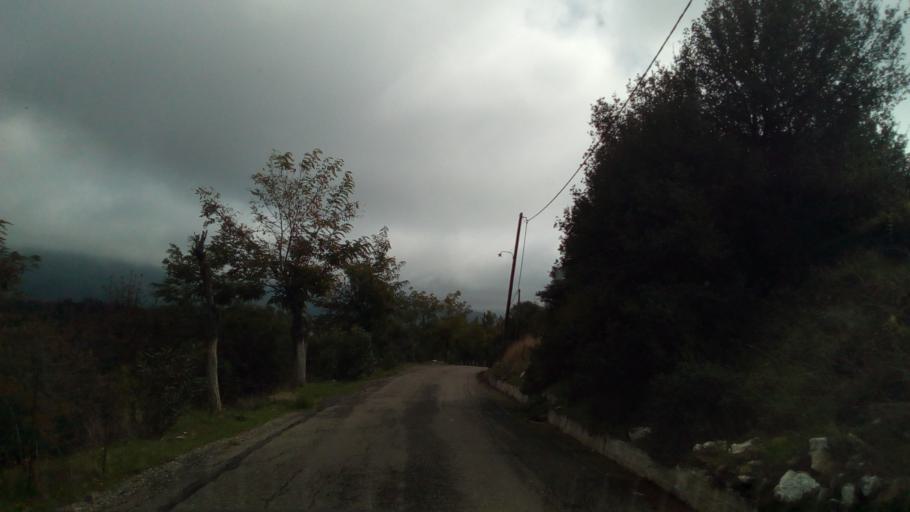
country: GR
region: West Greece
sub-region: Nomos Aitolias kai Akarnanias
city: Nafpaktos
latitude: 38.4475
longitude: 21.9666
